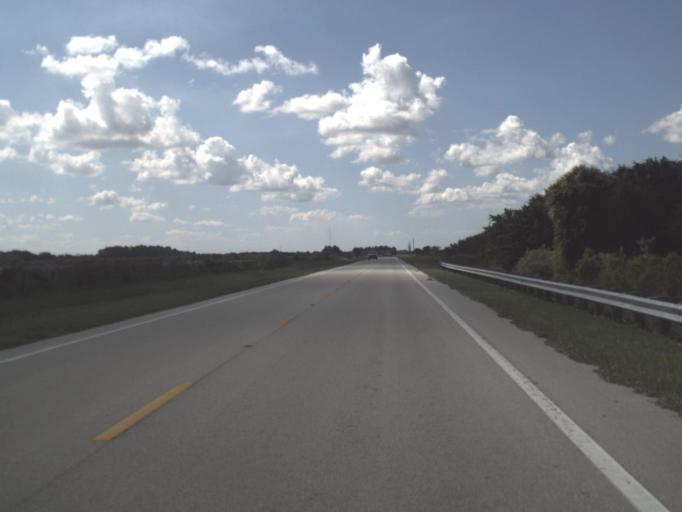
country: US
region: Florida
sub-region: Hendry County
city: Port LaBelle
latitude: 26.8123
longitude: -81.3790
